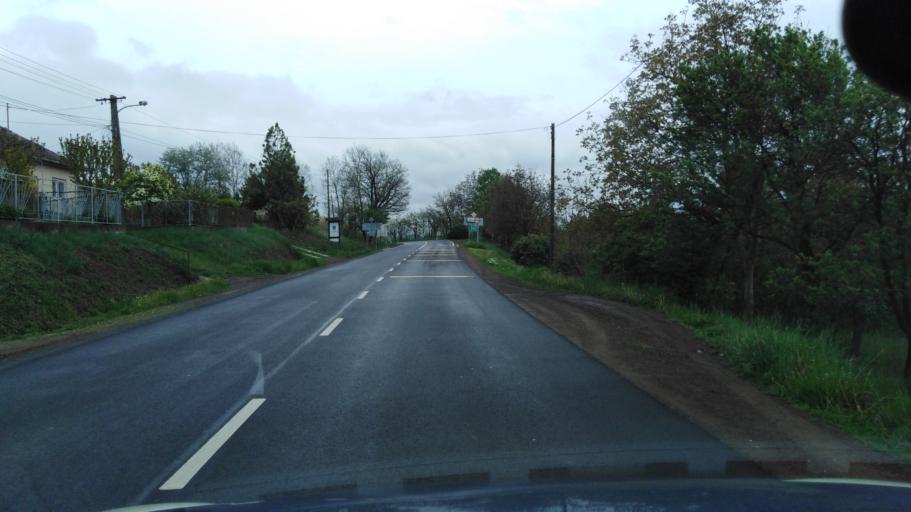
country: HU
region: Nograd
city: Karancskeszi
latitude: 48.1206
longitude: 19.6420
